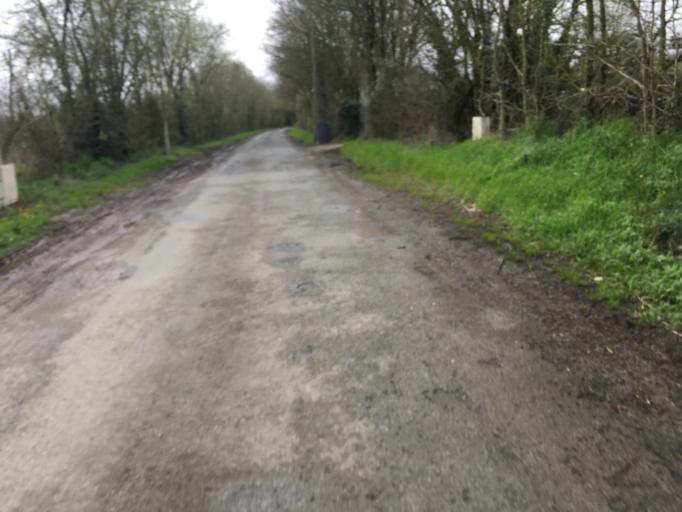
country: FR
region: Poitou-Charentes
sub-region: Departement de la Charente-Maritime
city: Saint-Germain-de-Marencennes
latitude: 46.1133
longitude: -0.8018
